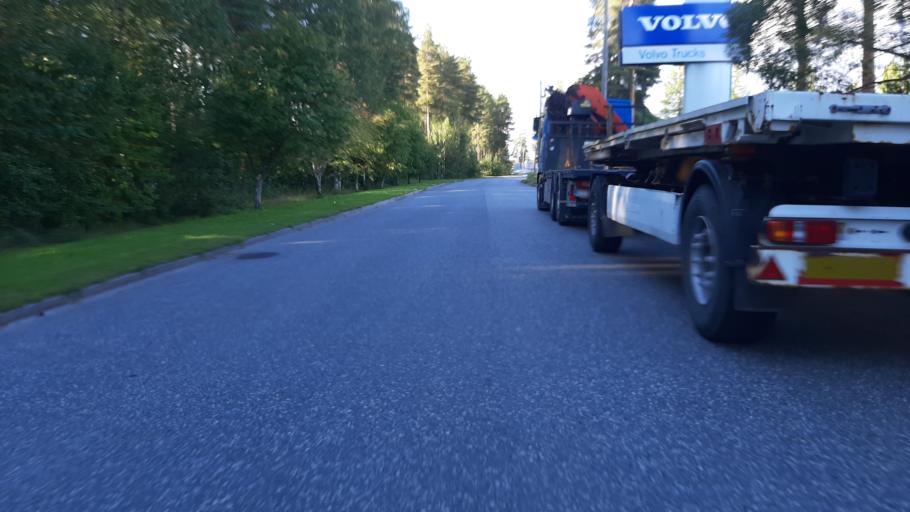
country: FI
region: North Karelia
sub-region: Joensuu
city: Joensuu
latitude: 62.6238
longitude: 29.7707
